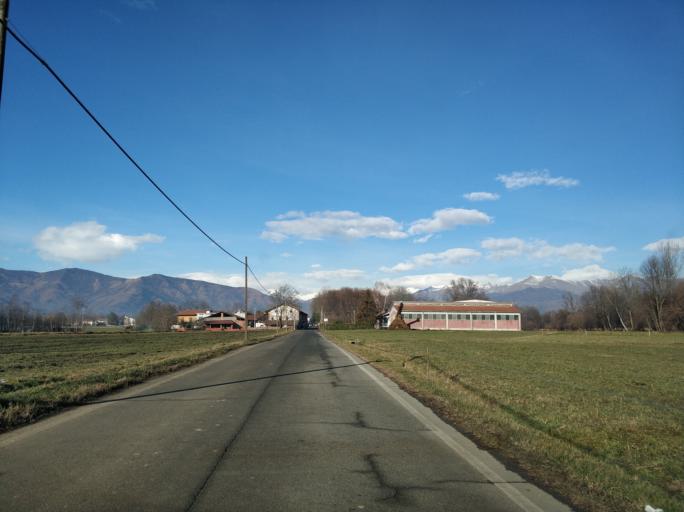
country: IT
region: Piedmont
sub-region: Provincia di Torino
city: Cirie
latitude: 45.2158
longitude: 7.5854
